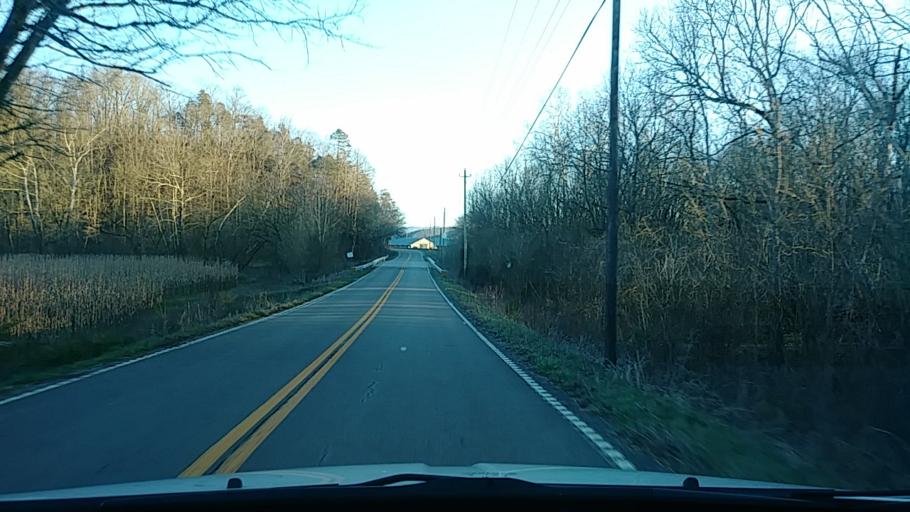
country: US
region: Tennessee
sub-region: Greene County
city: Mosheim
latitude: 36.1254
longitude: -83.0939
